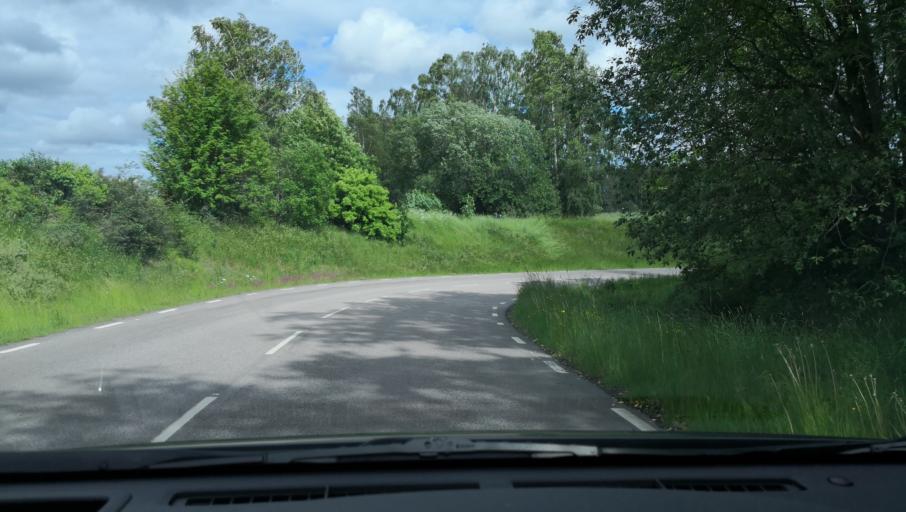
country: SE
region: OErebro
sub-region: Lindesbergs Kommun
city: Fellingsbro
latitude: 59.3533
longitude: 15.6678
